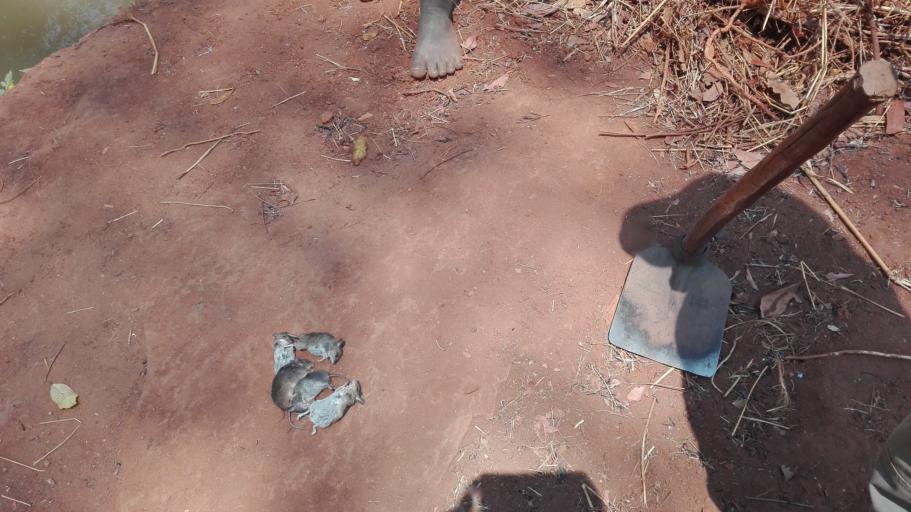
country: MZ
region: Nampula
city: Mutuali
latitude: -15.6851
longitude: 37.1686
